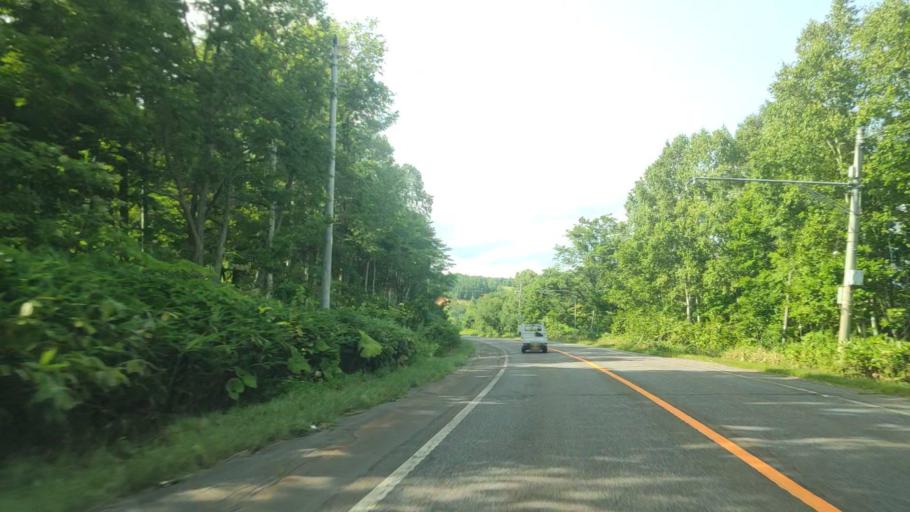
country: JP
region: Hokkaido
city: Nayoro
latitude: 44.3905
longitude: 142.3972
